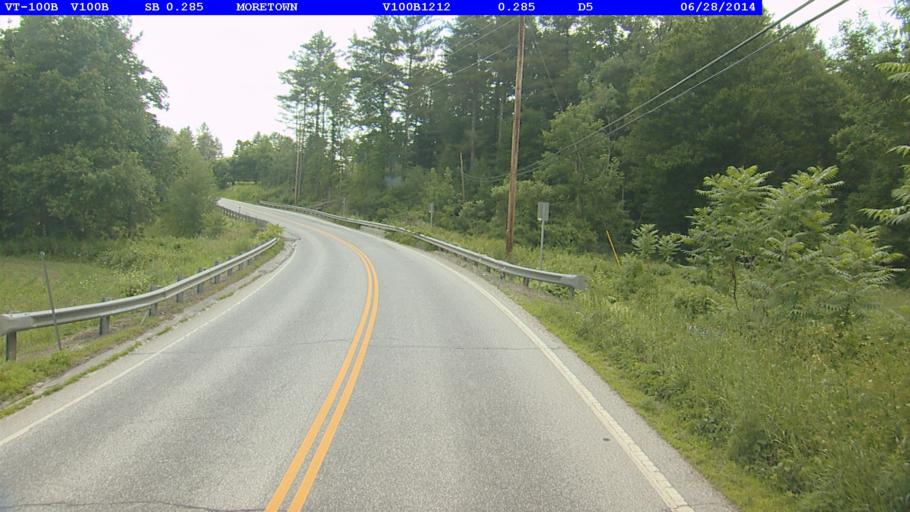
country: US
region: Vermont
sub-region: Washington County
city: Waterbury
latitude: 44.2442
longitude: -72.7744
